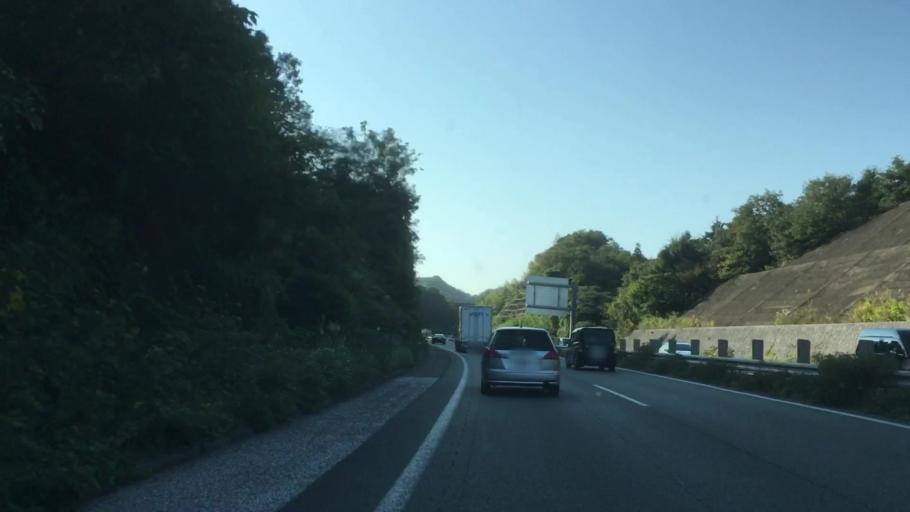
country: JP
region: Yamaguchi
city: Ogori-shimogo
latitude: 34.1283
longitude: 131.3814
